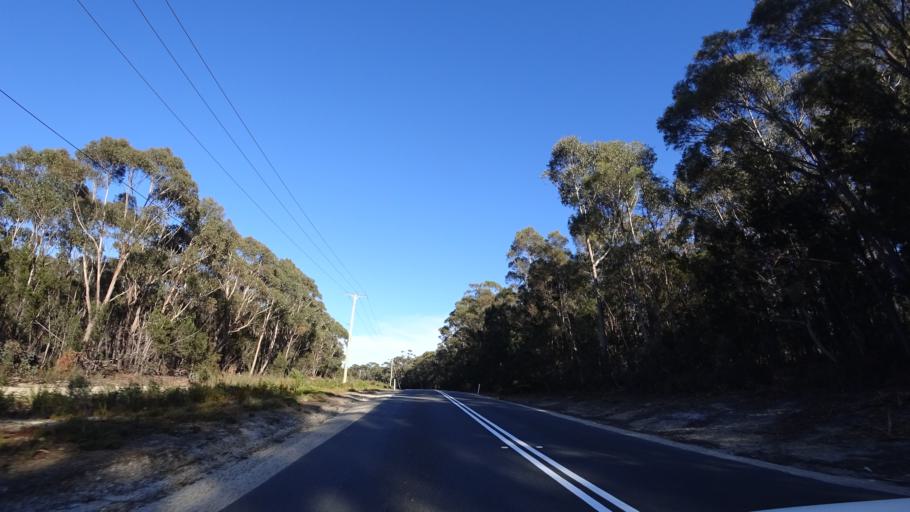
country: AU
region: Tasmania
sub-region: Break O'Day
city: St Helens
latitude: -41.2836
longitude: 148.1566
